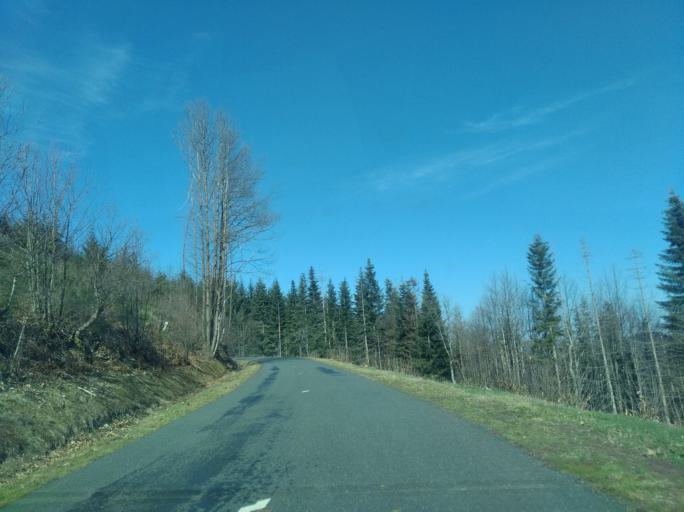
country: FR
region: Auvergne
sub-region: Departement de l'Allier
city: Le Mayet-de-Montagne
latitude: 46.1016
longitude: 3.7404
